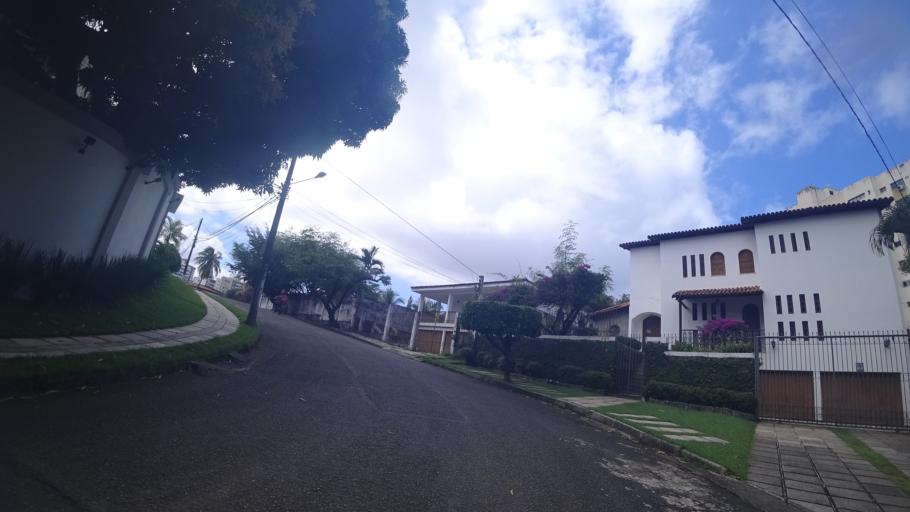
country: BR
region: Bahia
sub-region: Salvador
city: Salvador
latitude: -12.9928
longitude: -38.4637
